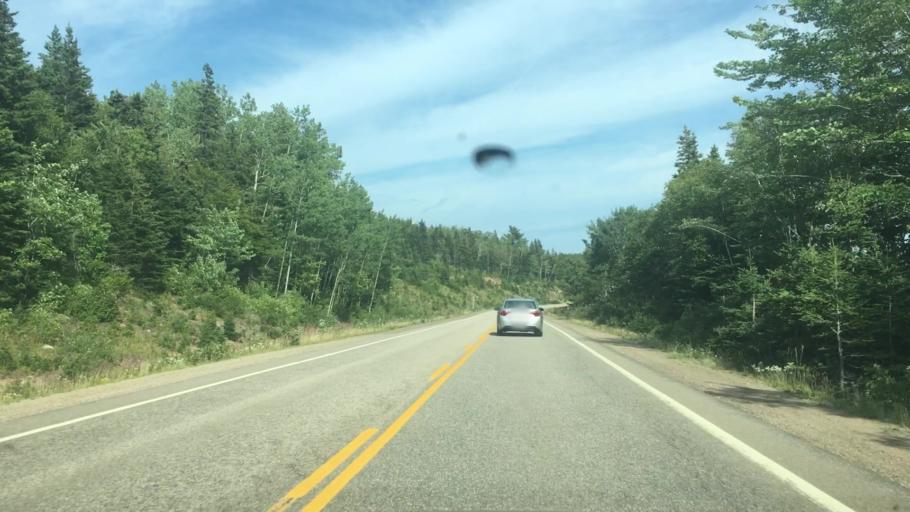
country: CA
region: Nova Scotia
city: Sydney Mines
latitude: 46.7135
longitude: -60.3592
